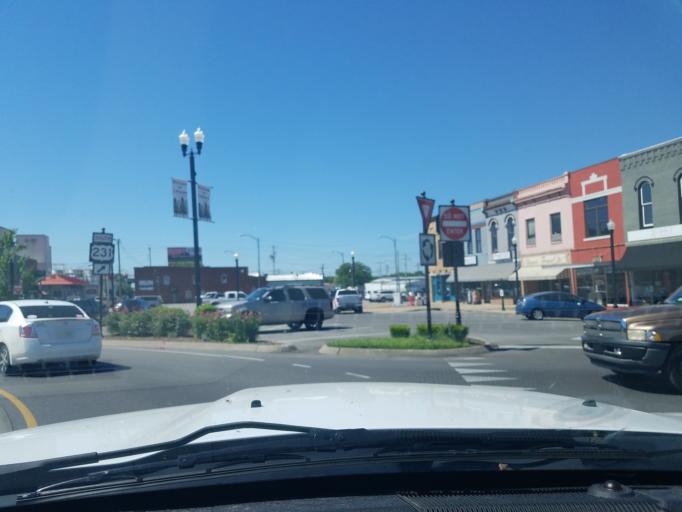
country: US
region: Tennessee
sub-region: Wilson County
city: Lebanon
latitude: 36.2080
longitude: -86.2913
